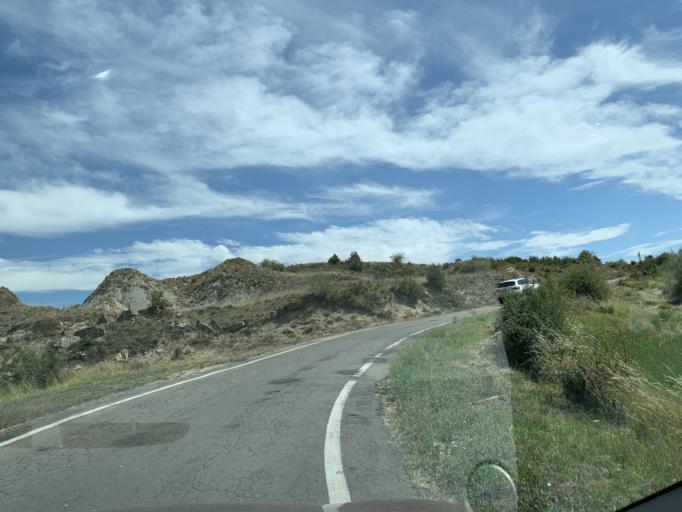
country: ES
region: Aragon
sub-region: Provincia de Huesca
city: Santa Cruz de la Seros
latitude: 42.5936
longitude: -0.6368
